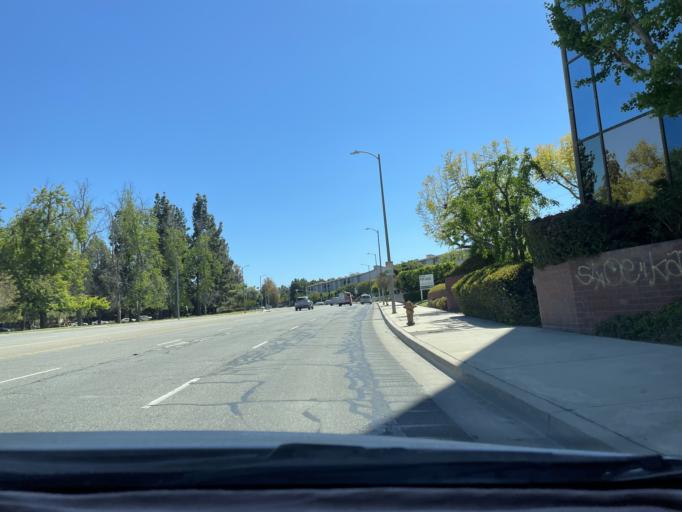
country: US
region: California
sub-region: Los Angeles County
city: Woodland Hills
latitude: 34.1772
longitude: -118.6051
